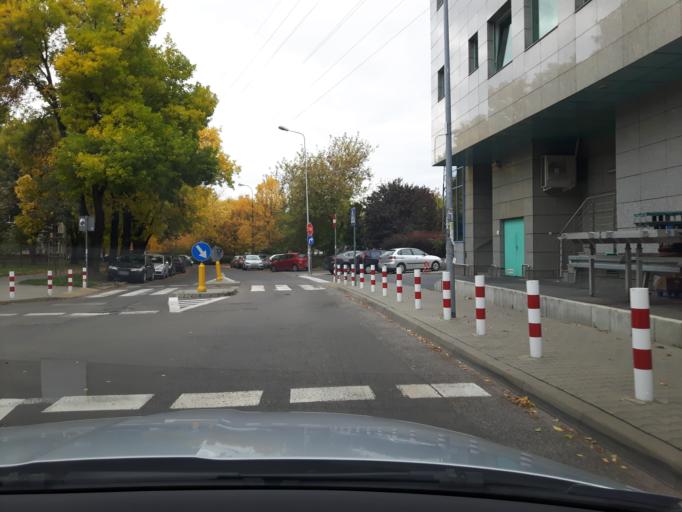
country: PL
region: Masovian Voivodeship
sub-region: Warszawa
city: Mokotow
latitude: 52.1740
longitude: 21.0036
